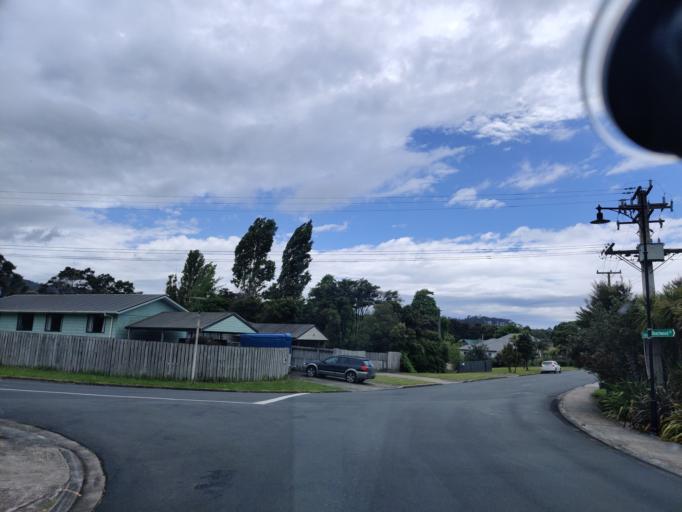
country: NZ
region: Auckland
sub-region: Auckland
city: Rothesay Bay
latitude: -36.5665
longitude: 174.6885
